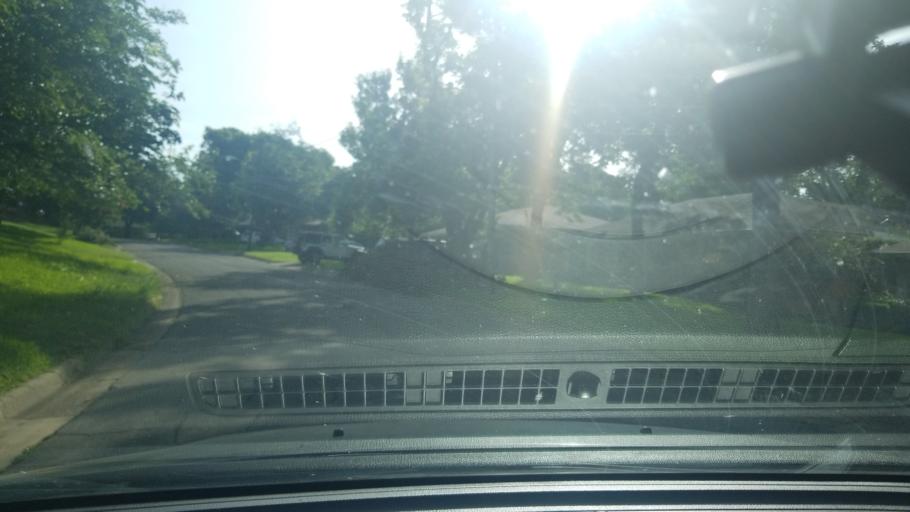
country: US
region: Texas
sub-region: Dallas County
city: Highland Park
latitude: 32.8005
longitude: -96.7035
